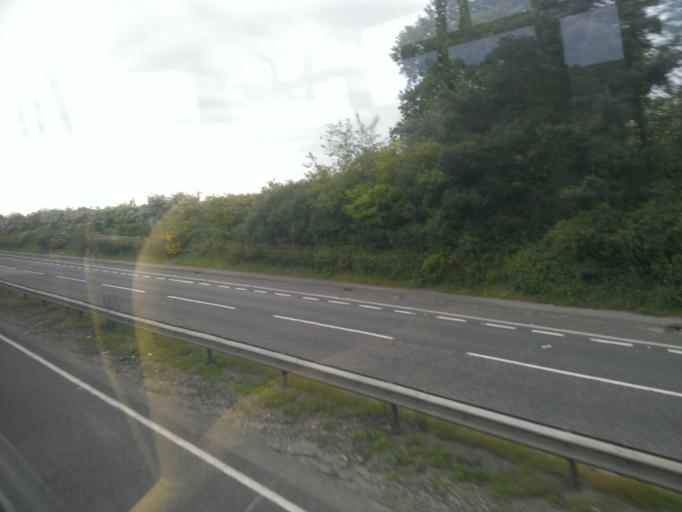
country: GB
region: England
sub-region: Suffolk
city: East Bergholt
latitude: 51.9437
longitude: 0.9560
